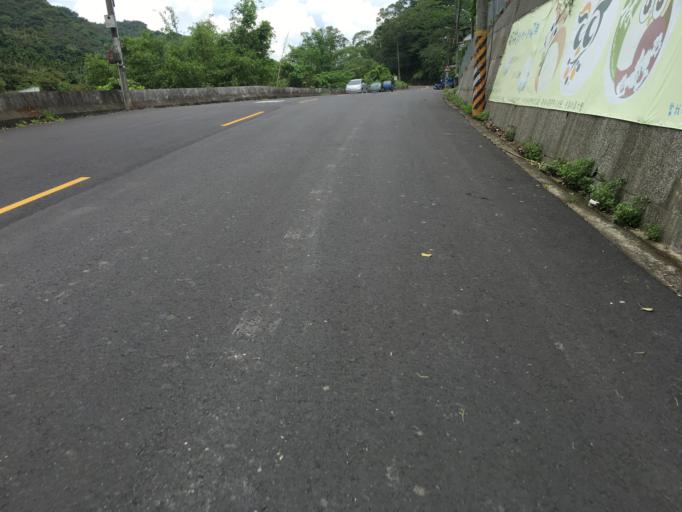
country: TW
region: Taiwan
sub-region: Taichung City
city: Taichung
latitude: 24.0632
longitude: 120.7376
